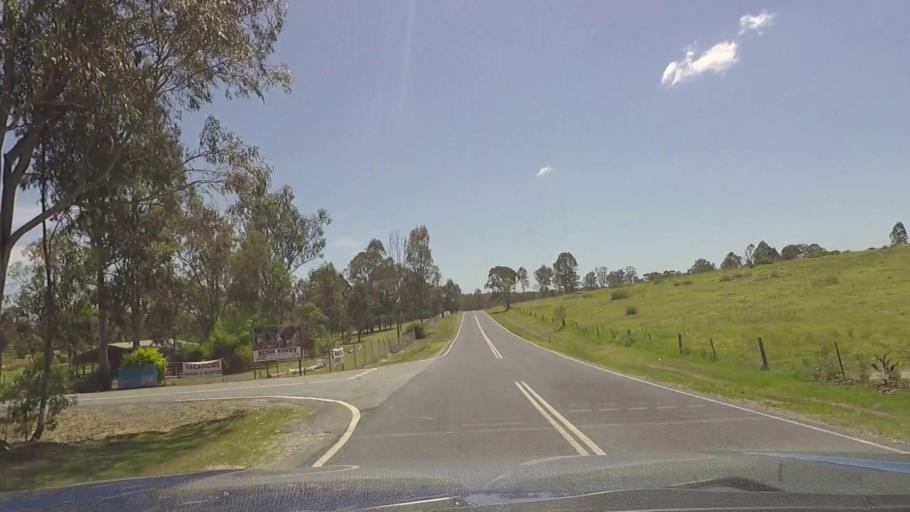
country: AU
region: Queensland
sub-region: Logan
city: North Maclean
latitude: -27.8259
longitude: 153.0256
